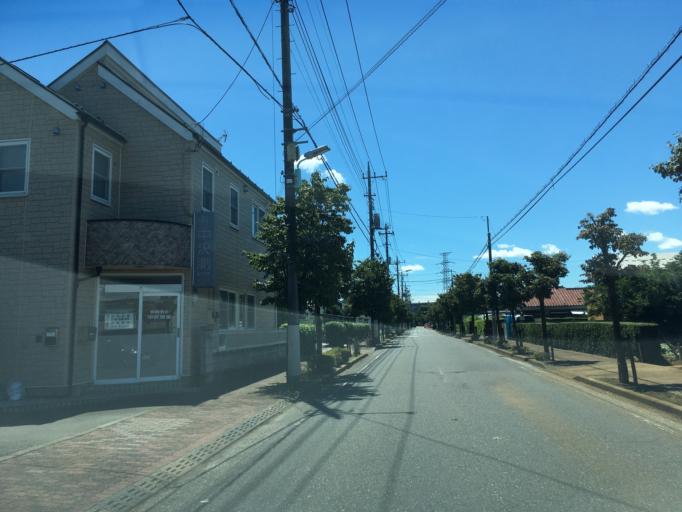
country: JP
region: Tokyo
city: Higashimurayama-shi
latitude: 35.7552
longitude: 139.4506
